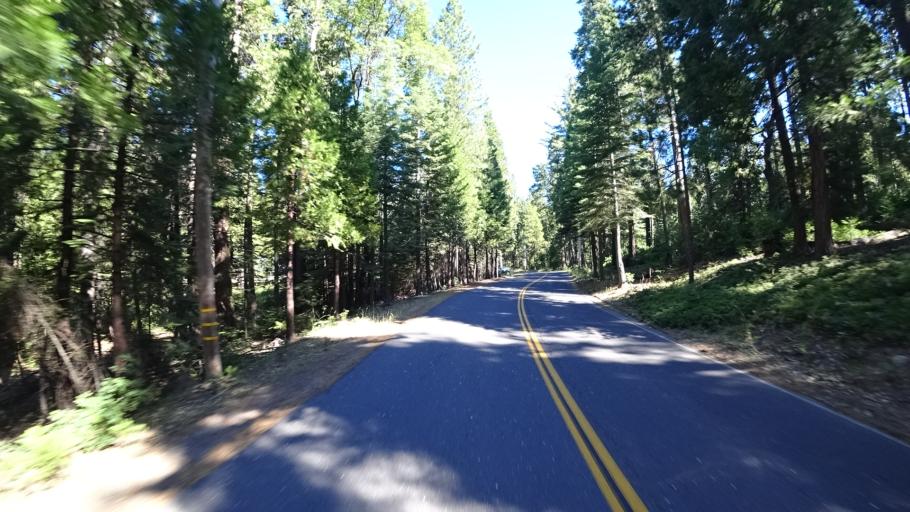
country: US
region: California
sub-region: Calaveras County
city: Arnold
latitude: 38.2991
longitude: -120.2662
